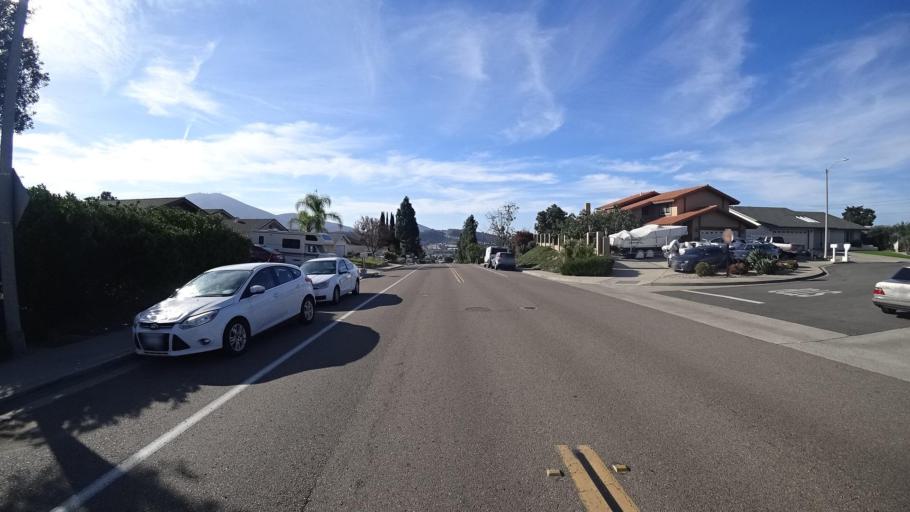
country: US
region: California
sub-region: San Diego County
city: Casa de Oro-Mount Helix
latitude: 32.7374
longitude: -116.9612
